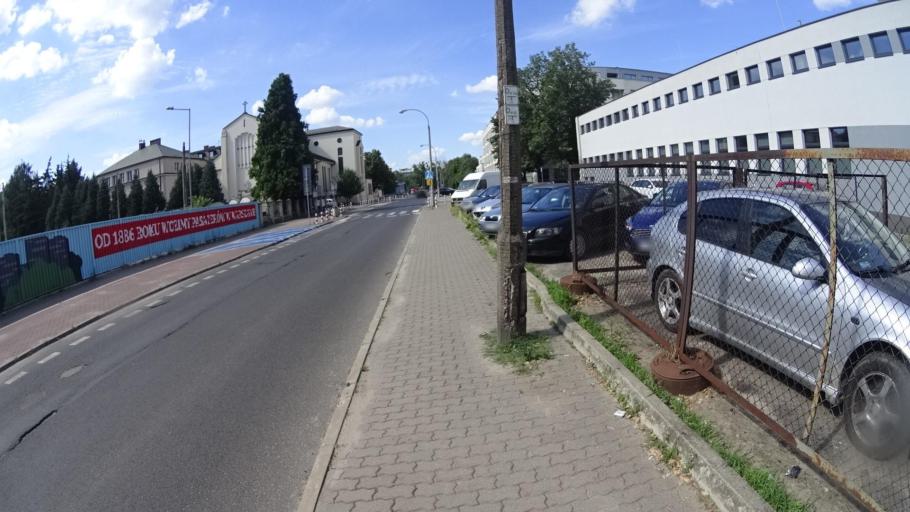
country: PL
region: Masovian Voivodeship
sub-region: Warszawa
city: Wola
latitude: 52.2335
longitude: 20.9771
